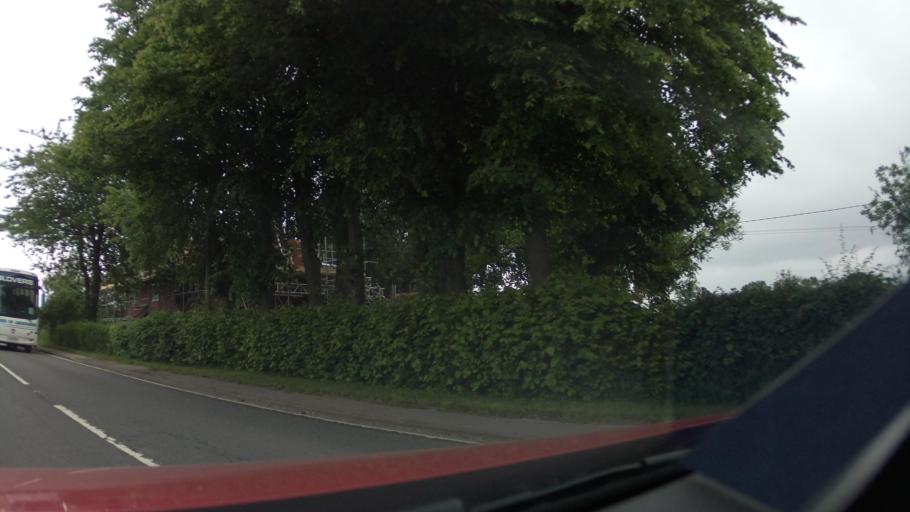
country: GB
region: England
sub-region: Derbyshire
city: Yeldersley
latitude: 52.9602
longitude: -1.5972
